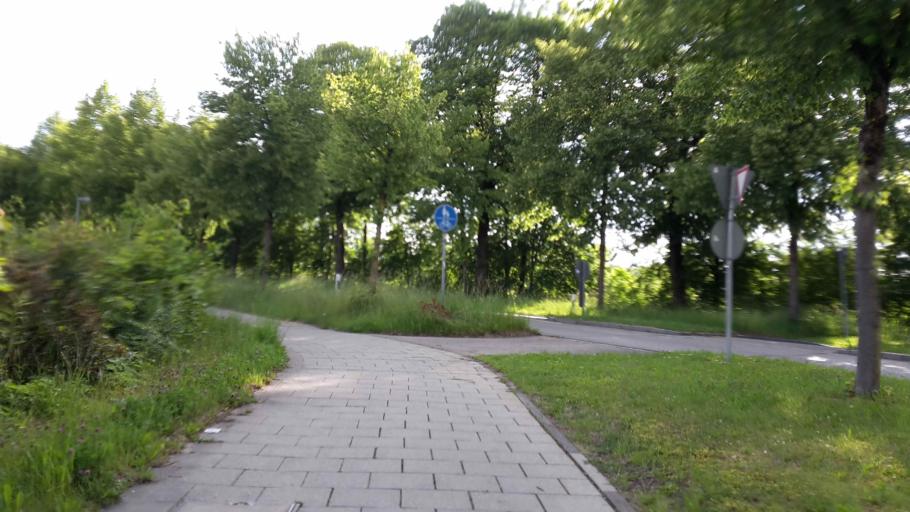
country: DE
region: Bavaria
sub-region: Upper Bavaria
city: Unterfoehring
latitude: 48.2116
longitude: 11.6586
